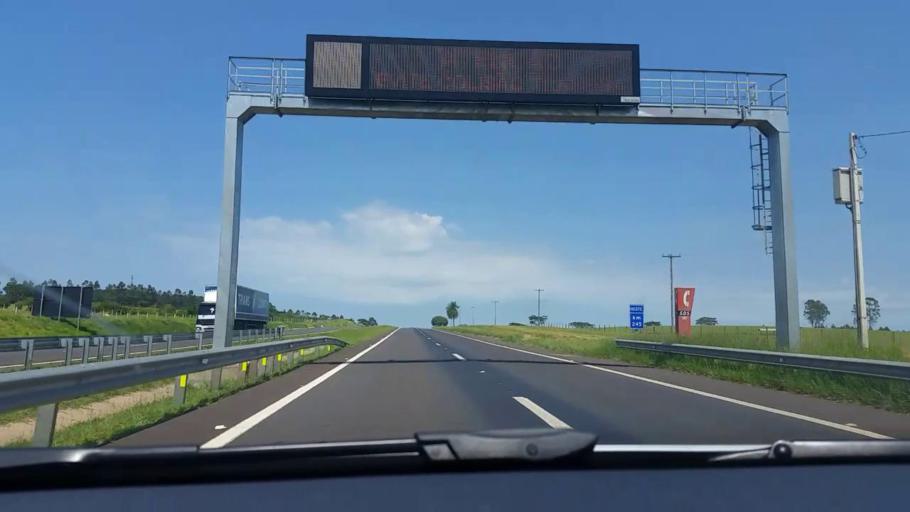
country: BR
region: Sao Paulo
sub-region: Bauru
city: Bauru
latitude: -22.4193
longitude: -49.1149
